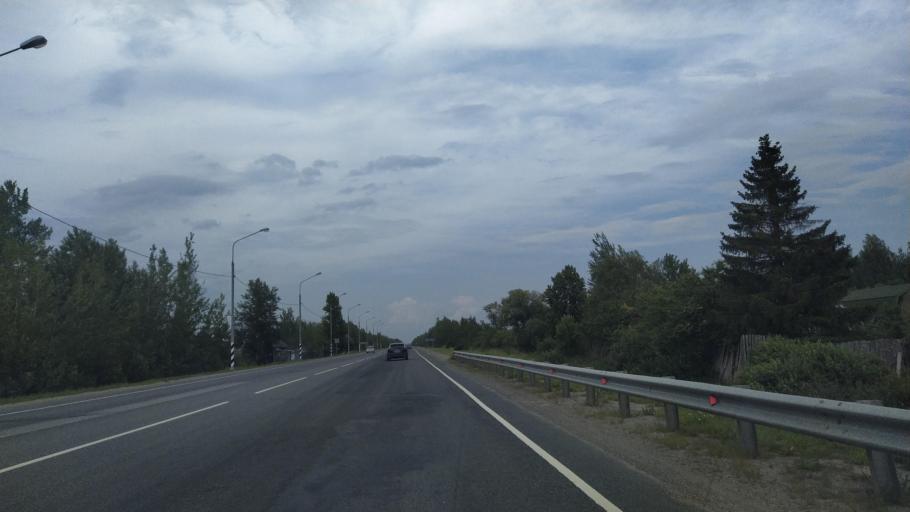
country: RU
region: Novgorod
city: Pankovka
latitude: 58.4507
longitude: 31.1335
